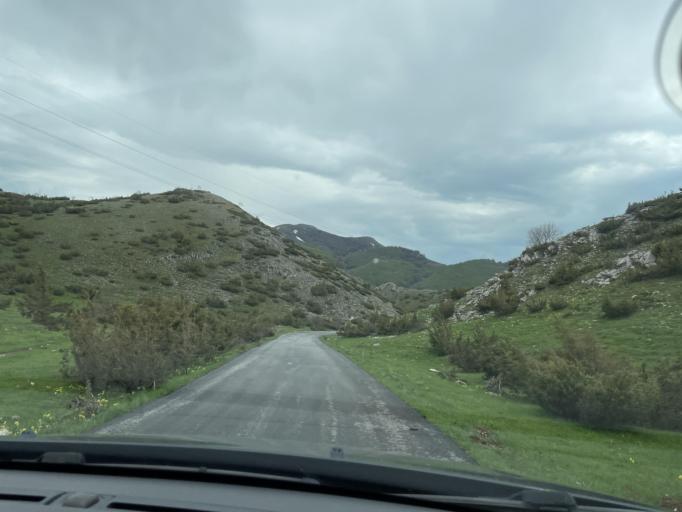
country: MK
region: Opstina Rostusa
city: Rostusha
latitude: 41.6106
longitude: 20.6800
